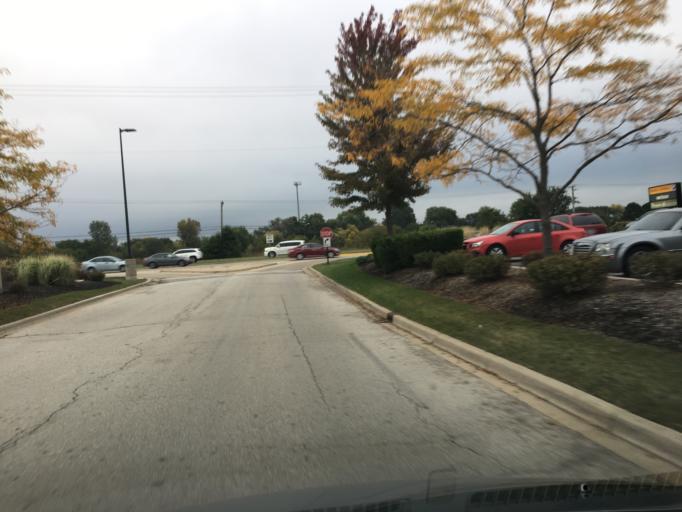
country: US
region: Illinois
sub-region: Will County
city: Plainfield
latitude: 41.6535
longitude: -88.2044
